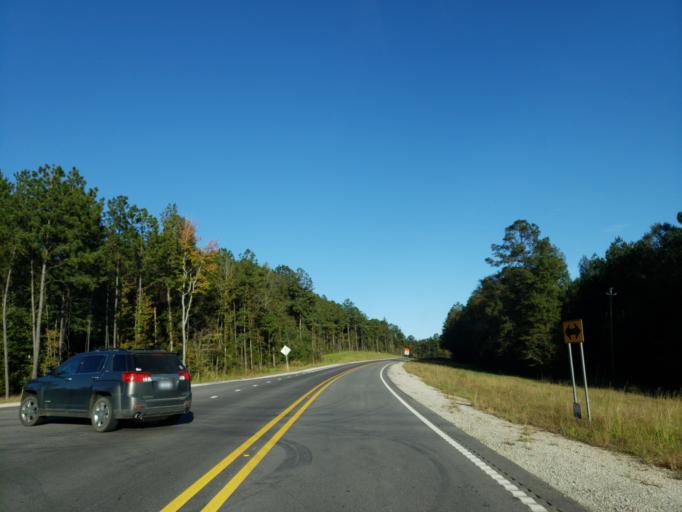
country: US
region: Mississippi
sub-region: Perry County
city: Richton
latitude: 31.3743
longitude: -88.8382
